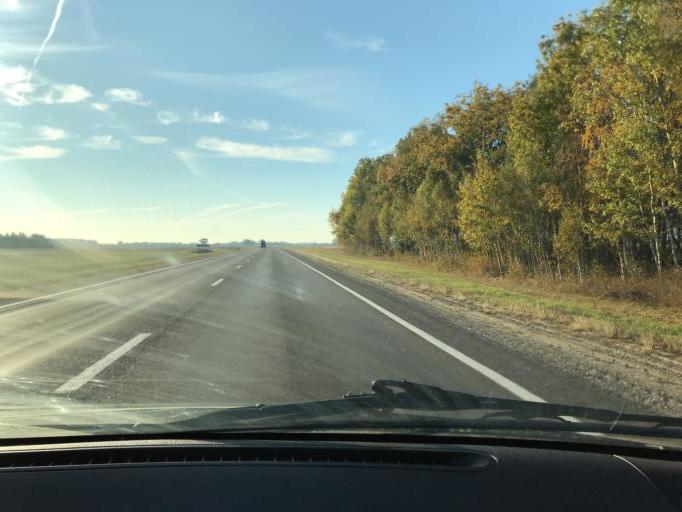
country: BY
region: Brest
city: Horad Kobryn
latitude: 52.2179
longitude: 24.5397
